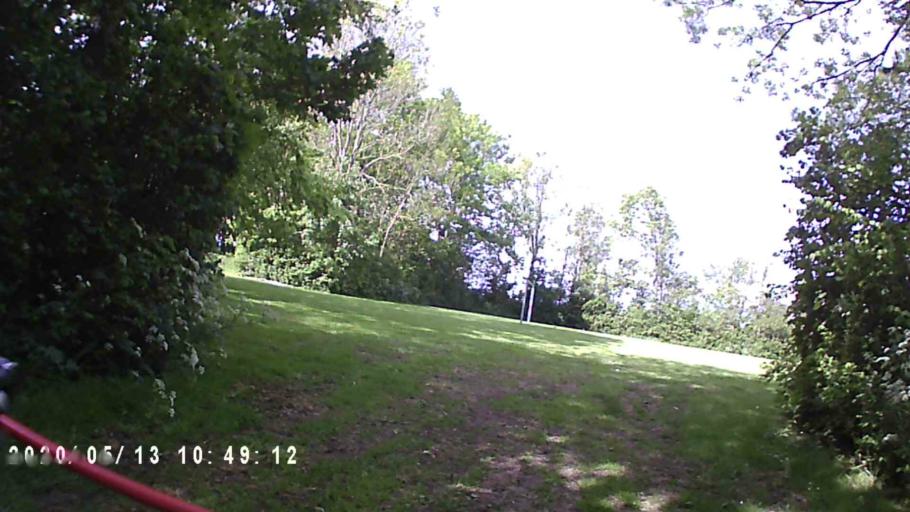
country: NL
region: Groningen
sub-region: Gemeente Zuidhorn
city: Grijpskerk
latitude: 53.2683
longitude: 6.3373
